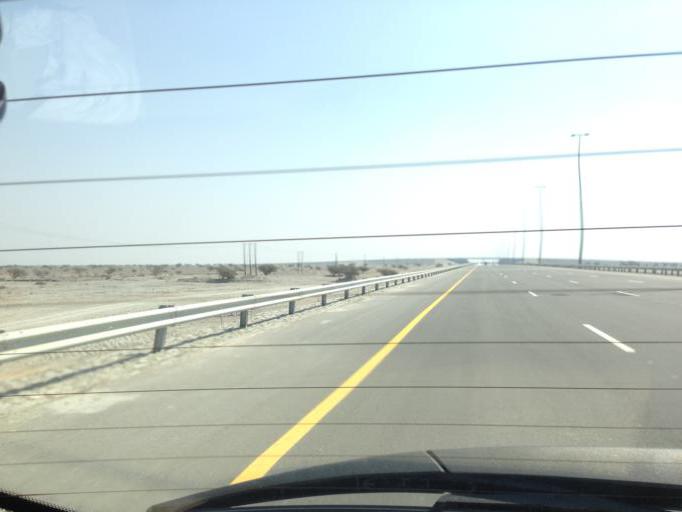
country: OM
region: Al Batinah
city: Barka'
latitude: 23.5758
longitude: 57.7605
